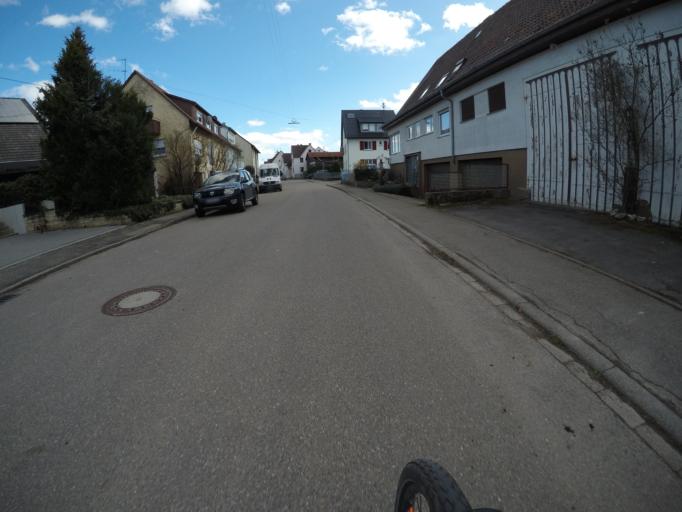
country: DE
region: Baden-Wuerttemberg
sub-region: Regierungsbezirk Stuttgart
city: Leinfelden-Echterdingen
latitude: 48.6710
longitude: 9.1621
